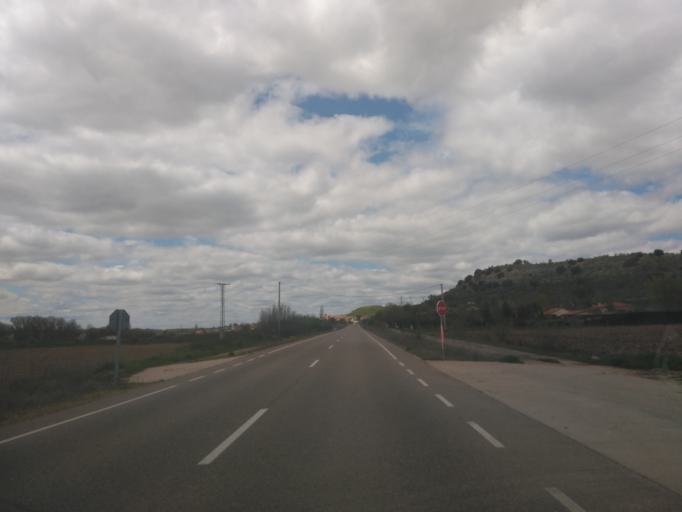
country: ES
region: Castille and Leon
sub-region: Provincia de Salamanca
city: Almenara de Tormes
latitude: 41.0587
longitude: -5.8069
